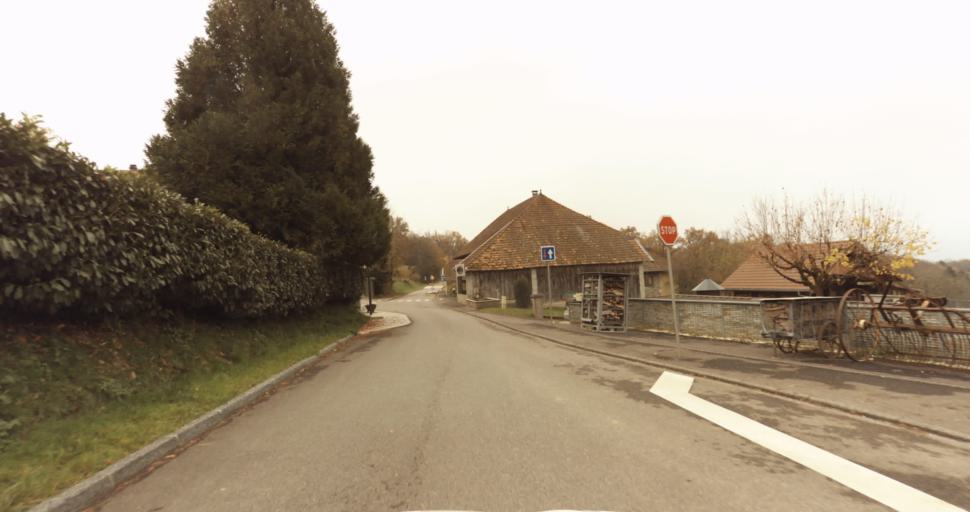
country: FR
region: Rhone-Alpes
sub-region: Departement de la Haute-Savoie
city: Saint-Felix
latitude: 45.7955
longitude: 5.9937
